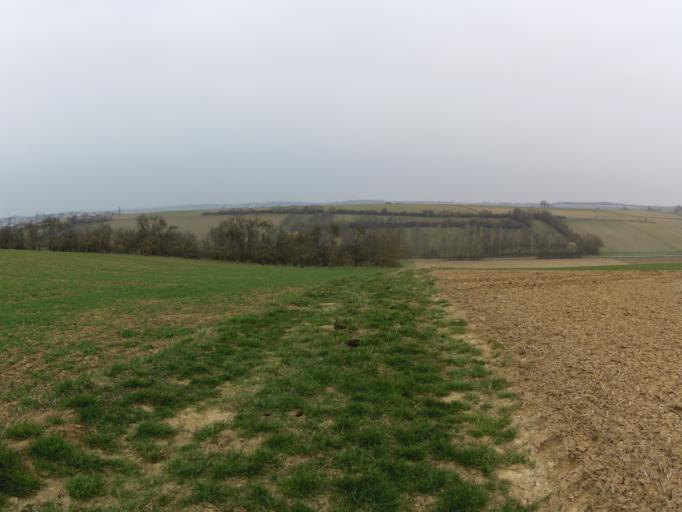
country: DE
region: Bavaria
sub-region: Regierungsbezirk Unterfranken
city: Estenfeld
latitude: 49.8184
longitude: 10.0174
